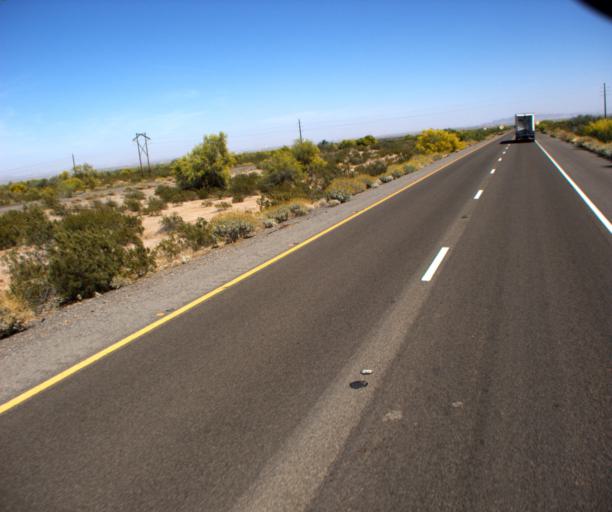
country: US
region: Arizona
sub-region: Pinal County
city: Maricopa
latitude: 32.8291
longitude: -112.0008
